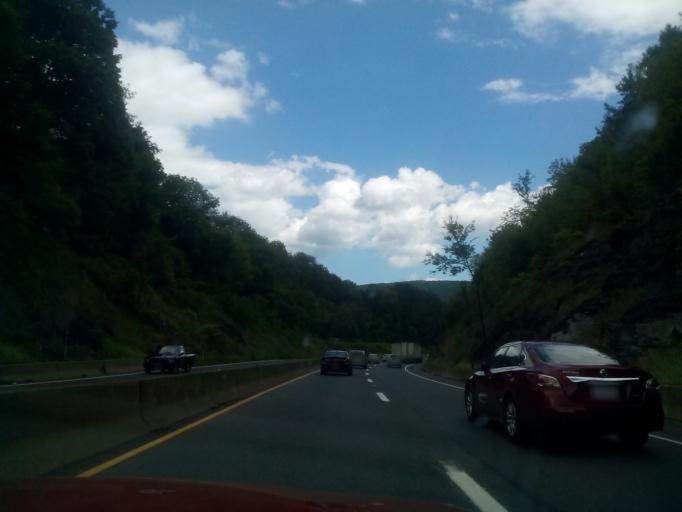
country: US
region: Pennsylvania
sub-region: Monroe County
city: East Stroudsburg
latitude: 40.9979
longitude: -75.1476
